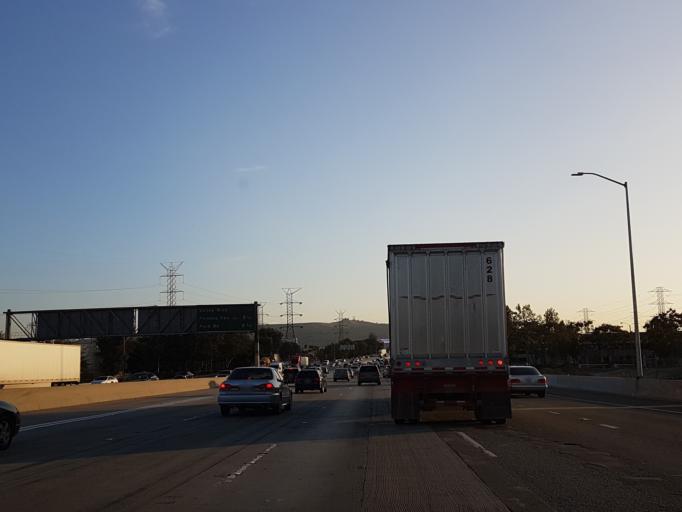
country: US
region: California
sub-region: Los Angeles County
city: Avocado Heights
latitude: 34.0611
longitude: -118.0011
